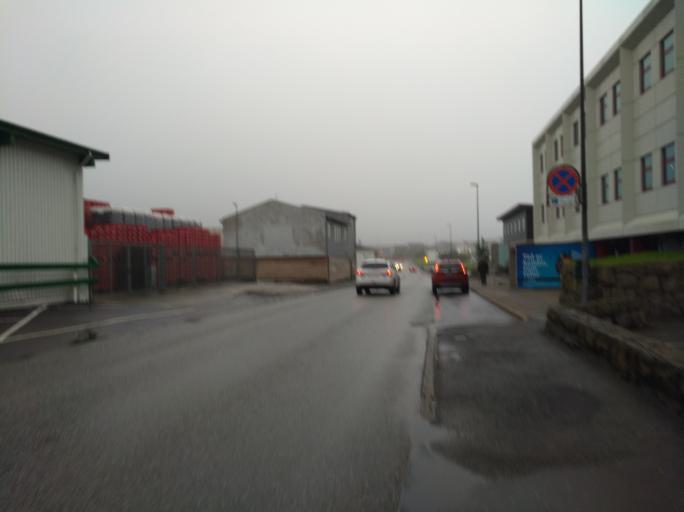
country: FO
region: Nordoyar
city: Klaksvik
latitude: 62.2264
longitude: -6.5886
